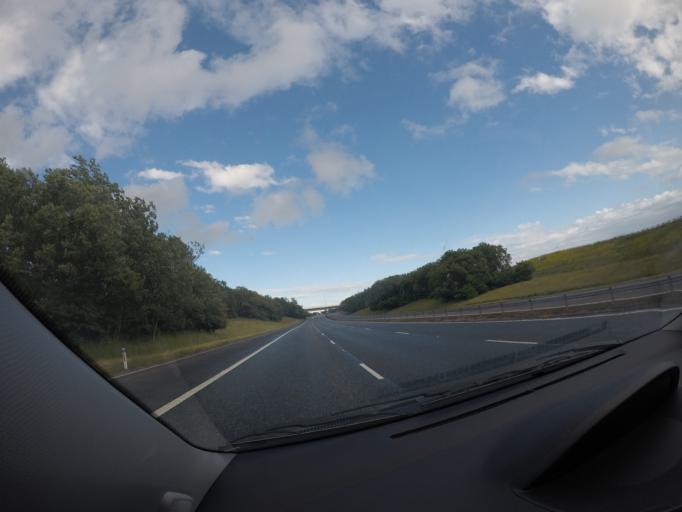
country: GB
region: Scotland
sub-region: Dumfries and Galloway
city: Annan
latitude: 55.0531
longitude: -3.2227
